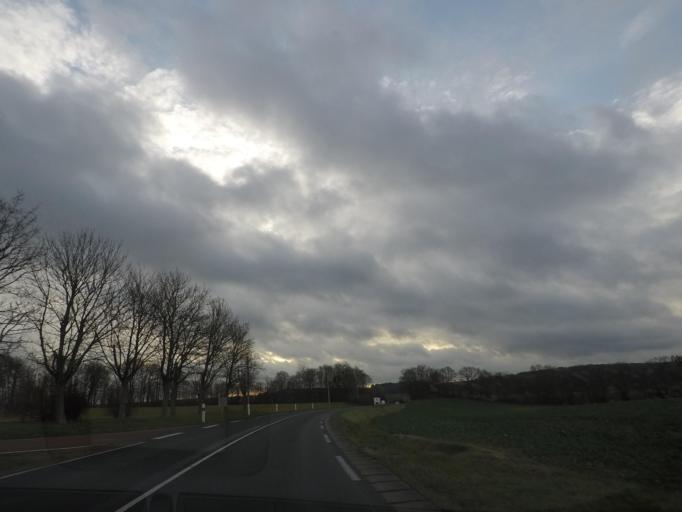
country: FR
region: Pays de la Loire
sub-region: Departement de la Sarthe
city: Vibraye
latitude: 48.1088
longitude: 0.7154
